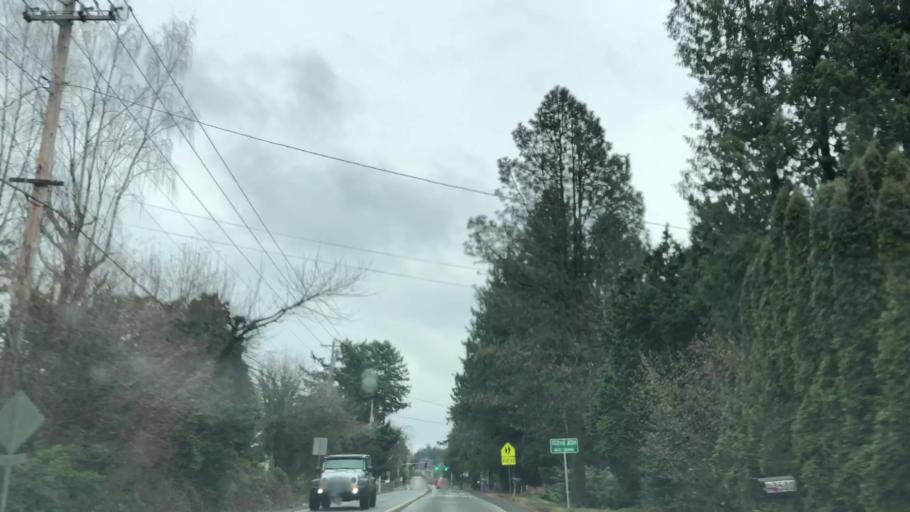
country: US
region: Oregon
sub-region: Washington County
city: West Haven
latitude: 45.5260
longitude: -122.7853
